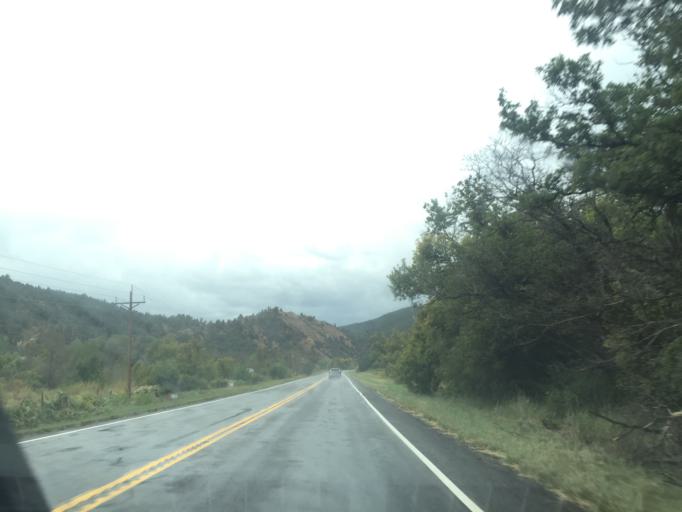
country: US
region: Utah
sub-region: Kane County
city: Kanab
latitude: 37.3498
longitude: -112.5986
